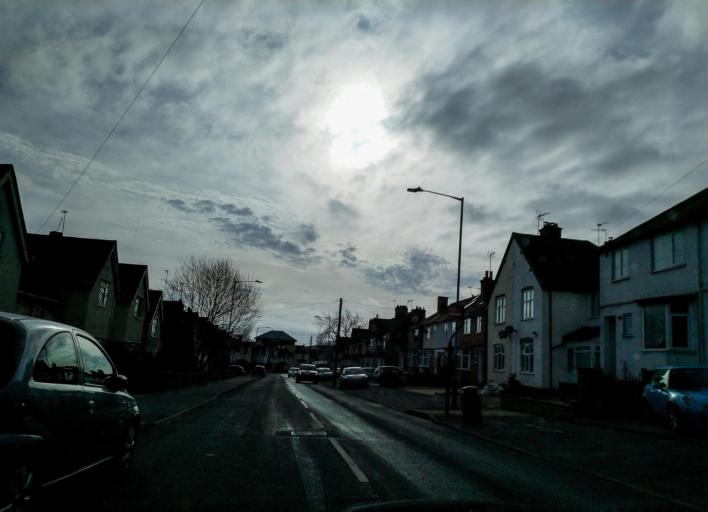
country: GB
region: England
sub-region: Warwickshire
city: Warwick
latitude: 52.2909
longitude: -1.5626
